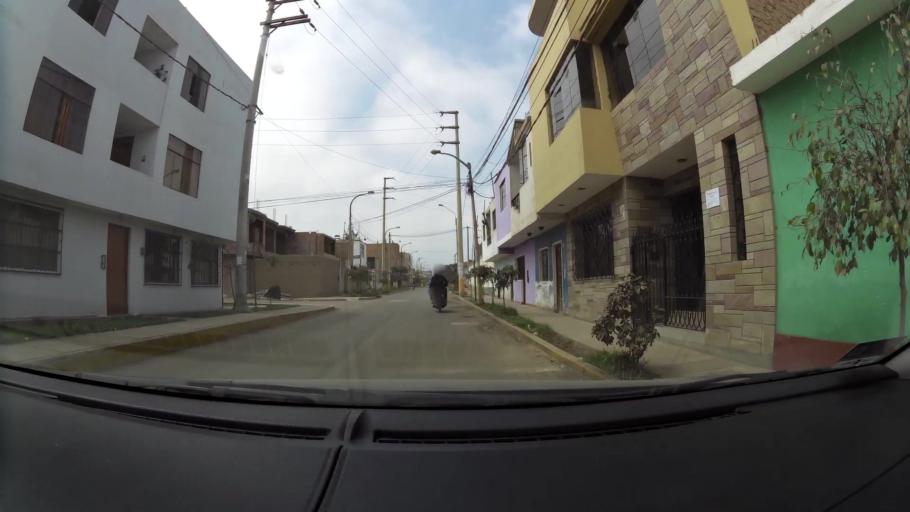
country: PE
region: Lima
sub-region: Provincia de Huaral
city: Huaral
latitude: -11.4939
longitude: -77.2173
